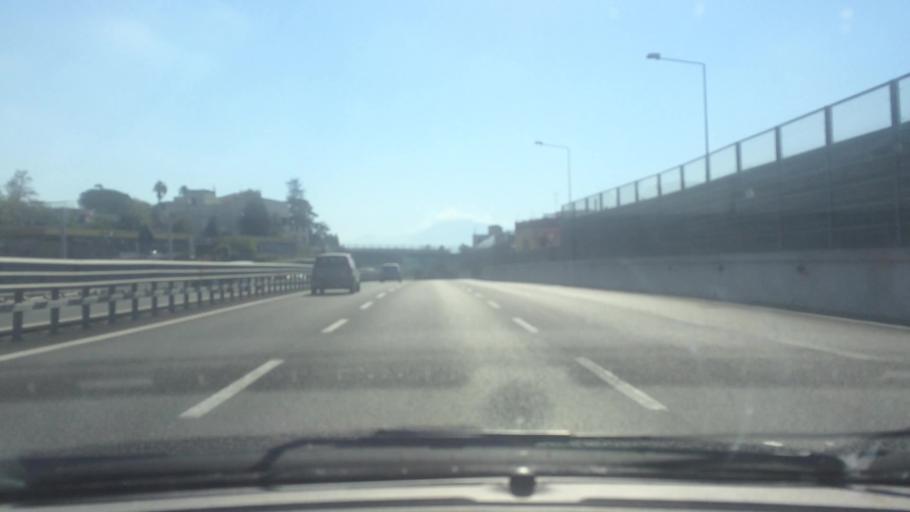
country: IT
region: Campania
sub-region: Provincia di Napoli
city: Ercolano
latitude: 40.8153
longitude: 14.3562
